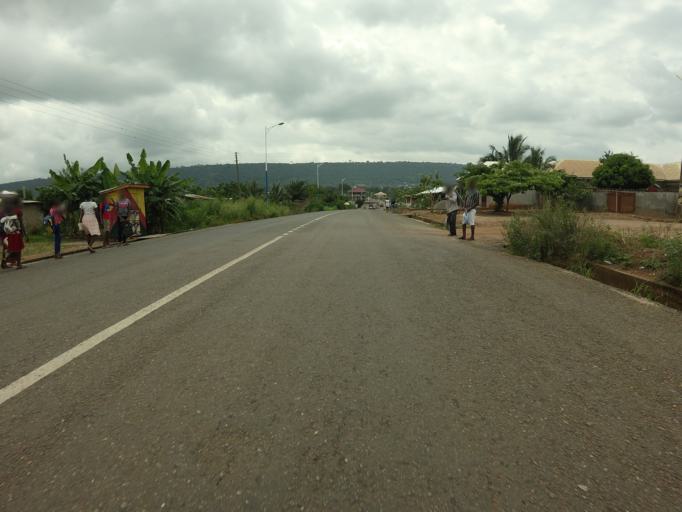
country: GH
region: Volta
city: Ho
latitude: 6.6258
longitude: 0.4900
